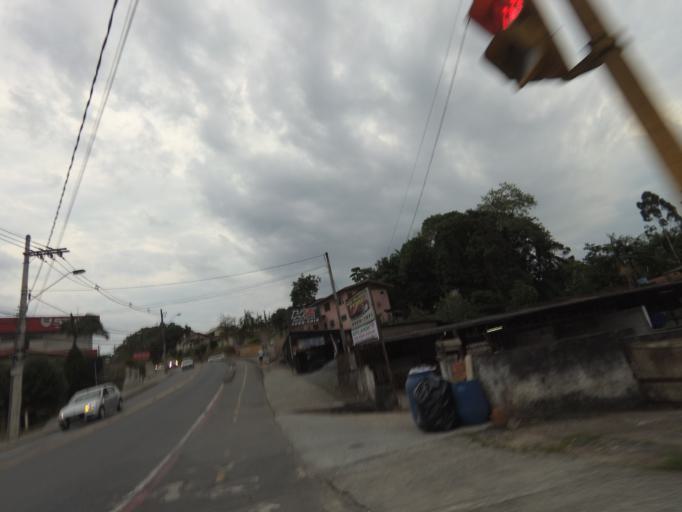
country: BR
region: Santa Catarina
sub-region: Blumenau
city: Blumenau
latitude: -26.8802
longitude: -49.0613
